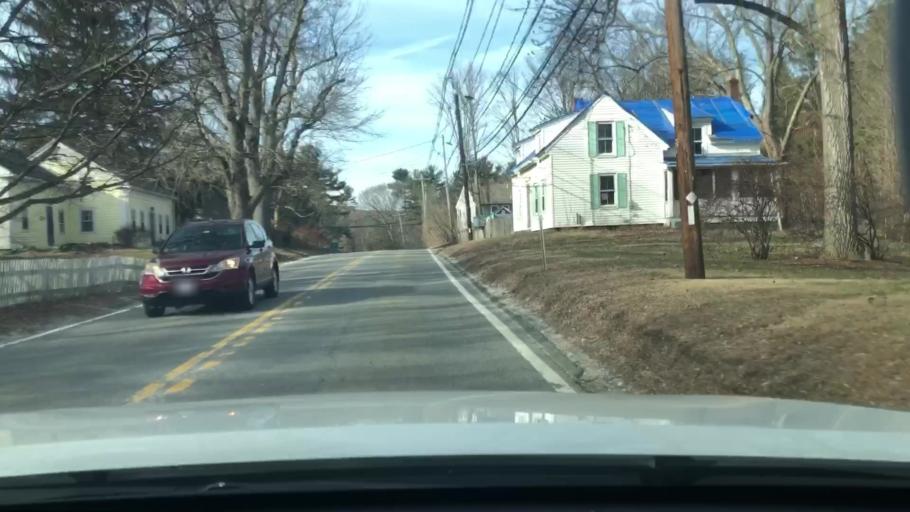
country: US
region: Massachusetts
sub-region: Worcester County
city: Upton
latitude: 42.1725
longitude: -71.5978
